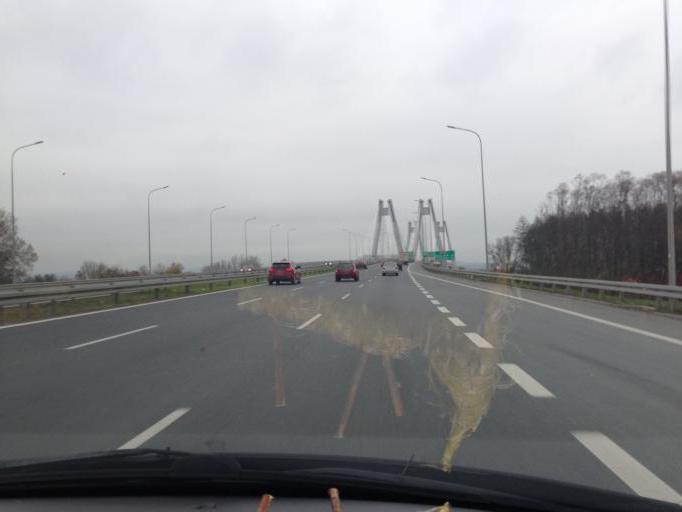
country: PL
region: Lesser Poland Voivodeship
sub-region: Powiat wielicki
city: Kokotow
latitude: 50.0563
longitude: 20.0744
